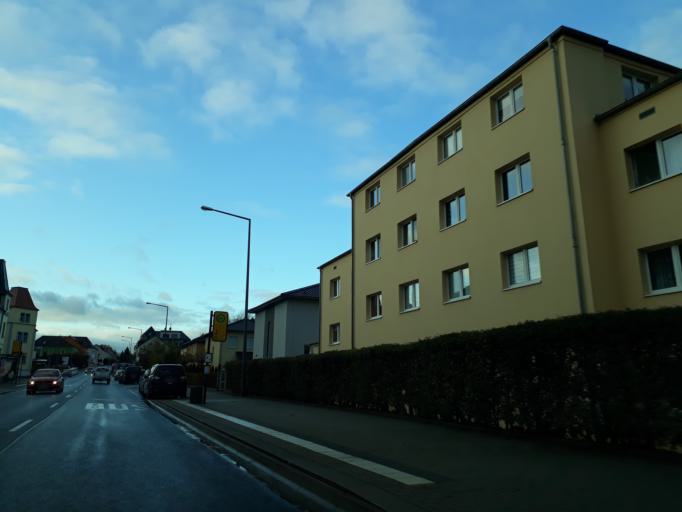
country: DE
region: Saxony
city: Bannewitz
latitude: 51.0063
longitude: 13.6888
